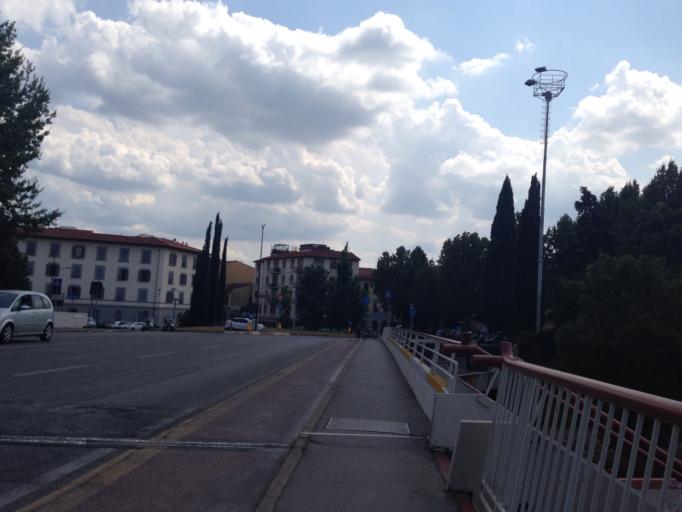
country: IT
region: Tuscany
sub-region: Province of Florence
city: Grassina Ponte a Ema
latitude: 43.7647
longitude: 11.2816
